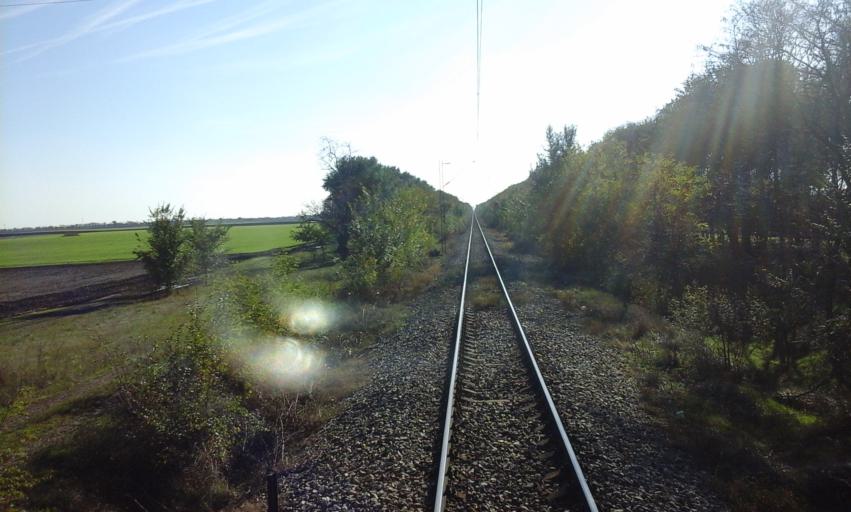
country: RS
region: Autonomna Pokrajina Vojvodina
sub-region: Severnobacki Okrug
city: Backa Topola
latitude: 45.8629
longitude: 19.6565
